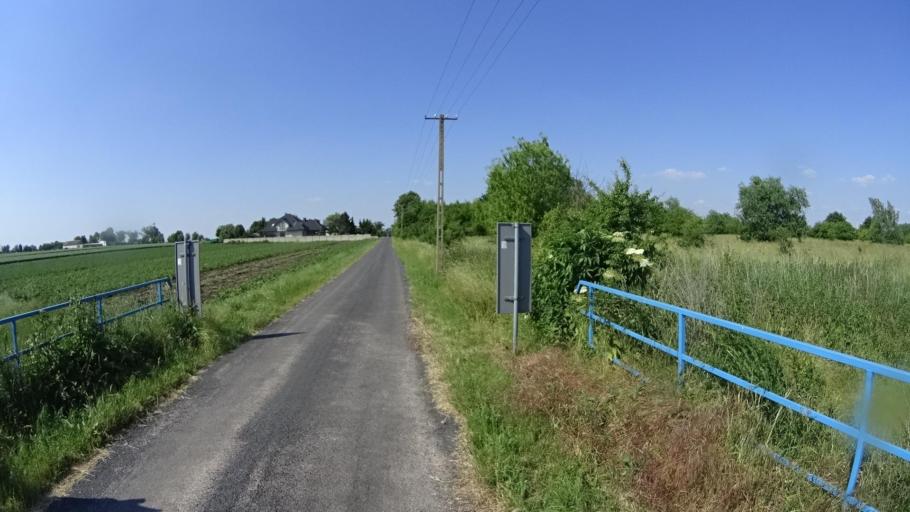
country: PL
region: Masovian Voivodeship
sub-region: Powiat grodziski
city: Milanowek
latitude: 52.1620
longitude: 20.6651
